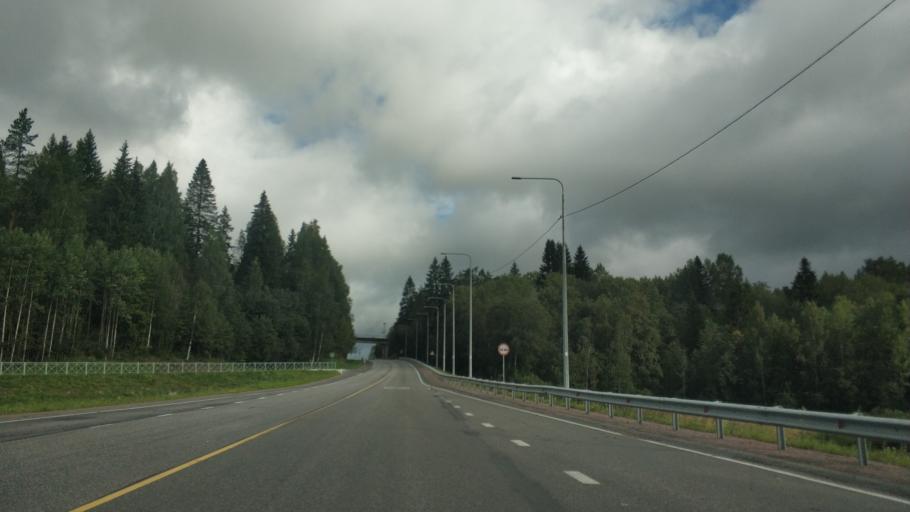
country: RU
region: Republic of Karelia
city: Khelyulya
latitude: 61.7760
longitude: 30.6617
